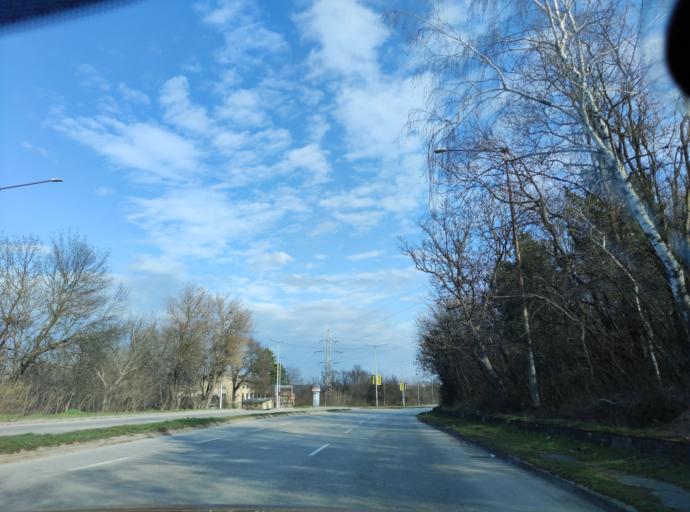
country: BG
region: Pleven
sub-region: Obshtina Pleven
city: Pleven
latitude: 43.4344
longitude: 24.5719
